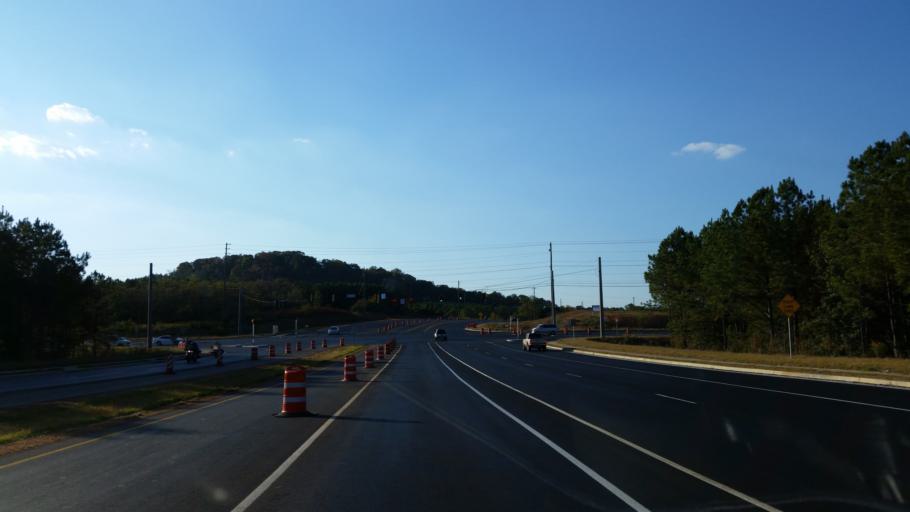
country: US
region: Georgia
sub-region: Bartow County
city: Cartersville
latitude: 34.2077
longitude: -84.7976
